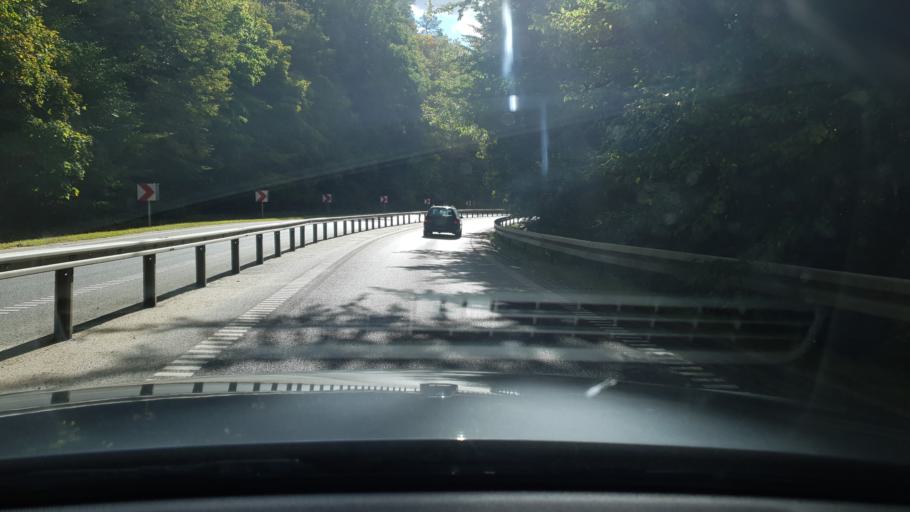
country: PL
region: Pomeranian Voivodeship
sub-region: Powiat wejherowski
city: Rekowo Dolne
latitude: 54.6282
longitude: 18.3437
